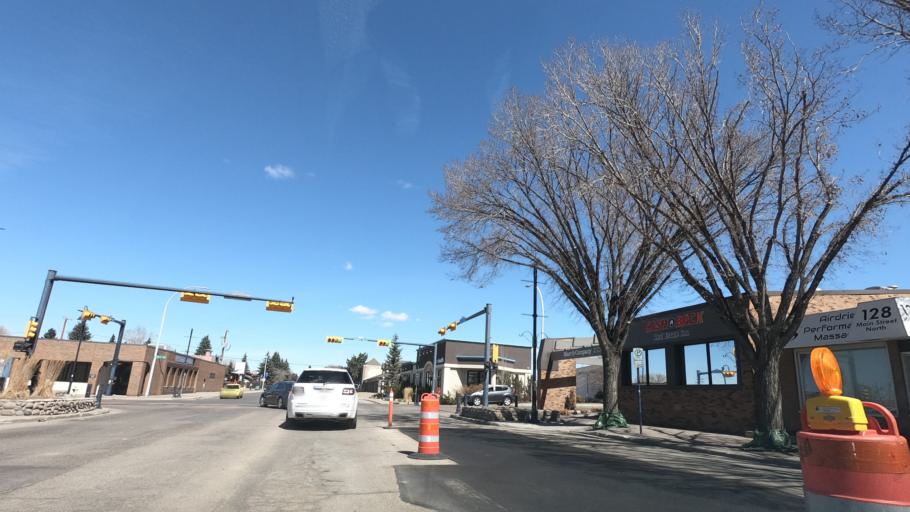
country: CA
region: Alberta
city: Airdrie
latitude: 51.2923
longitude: -114.0134
